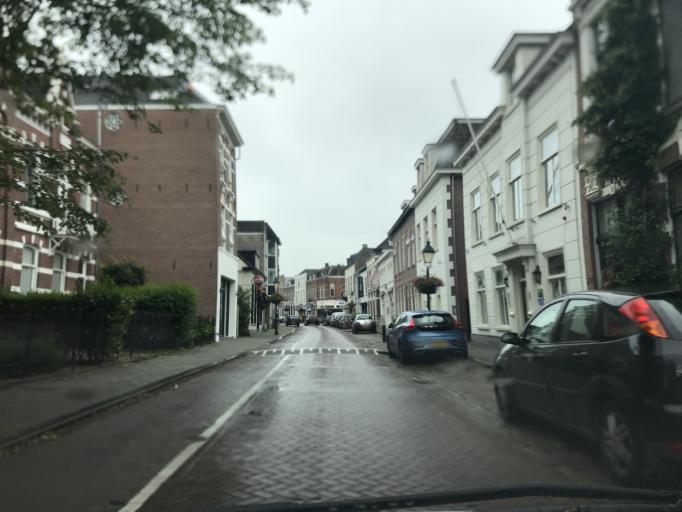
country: NL
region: North Brabant
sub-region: Gemeente Breda
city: Breda
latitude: 51.5716
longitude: 4.7837
